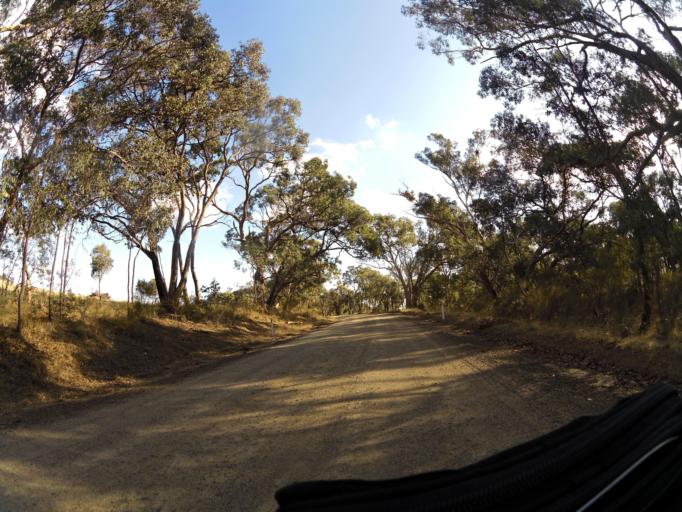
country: AU
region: Victoria
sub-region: Greater Bendigo
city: Kennington
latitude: -37.0212
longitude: 144.8016
